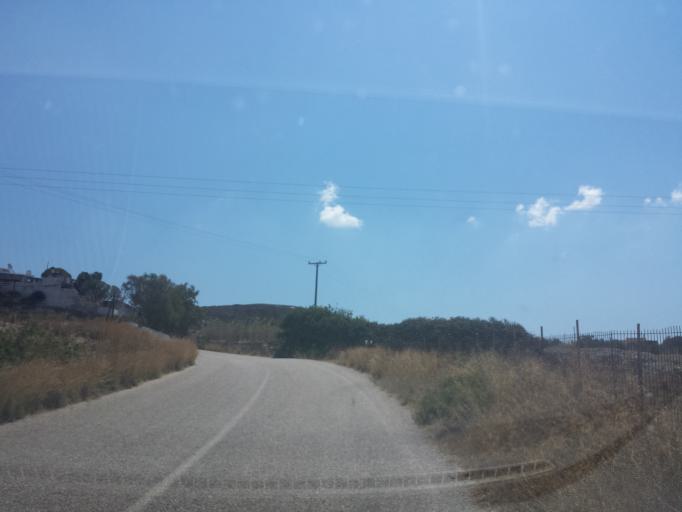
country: GR
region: South Aegean
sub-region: Nomos Kykladon
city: Adamas
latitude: 36.6879
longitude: 24.4971
